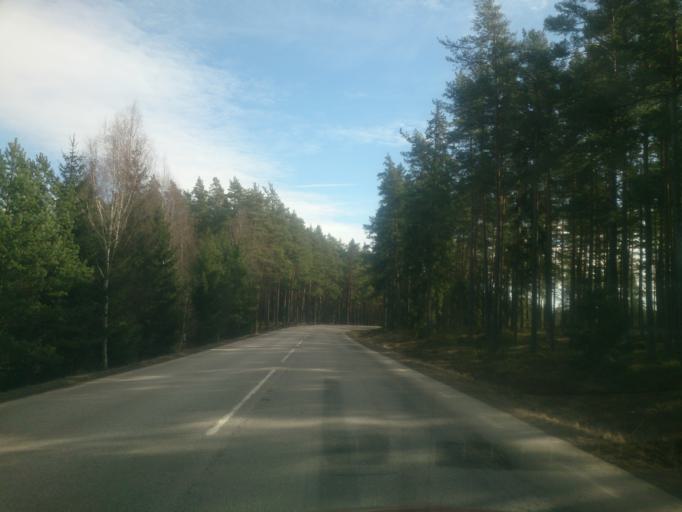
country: SE
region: OEstergoetland
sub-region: Finspangs Kommun
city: Finspang
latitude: 58.6640
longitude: 15.7749
